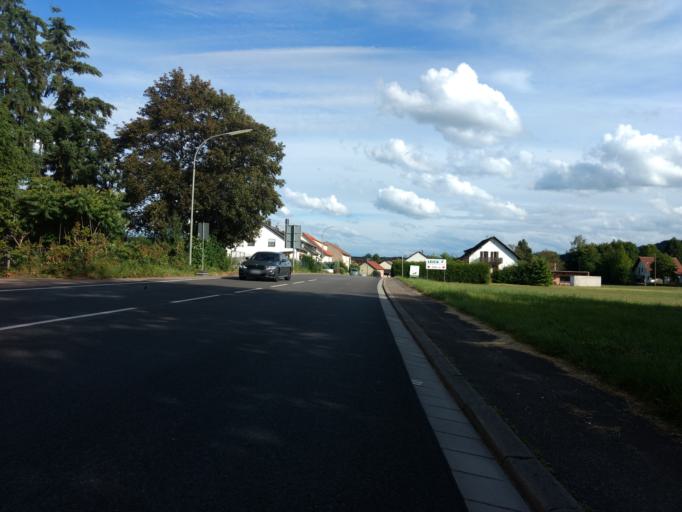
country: DE
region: Saarland
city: Mettlach
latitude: 49.4550
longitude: 6.6006
